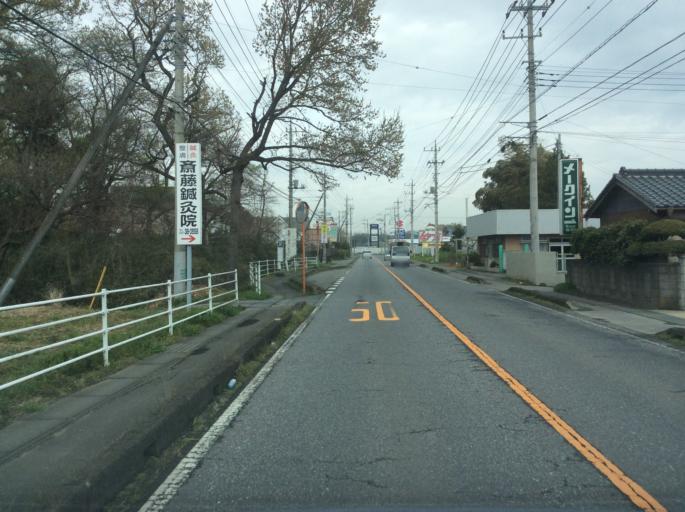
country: JP
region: Ibaraki
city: Iwai
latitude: 36.0151
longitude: 139.9061
